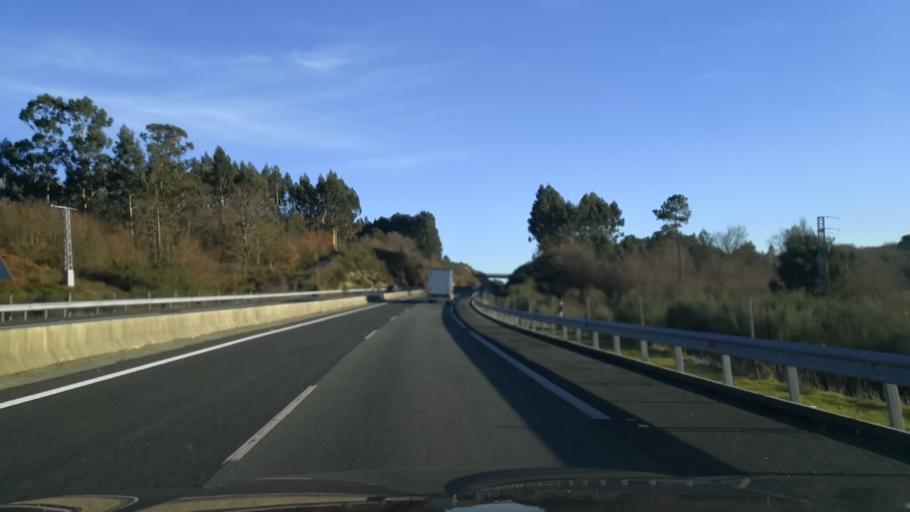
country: ES
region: Galicia
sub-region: Provincia de Ourense
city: Pinor
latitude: 42.4943
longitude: -8.0264
